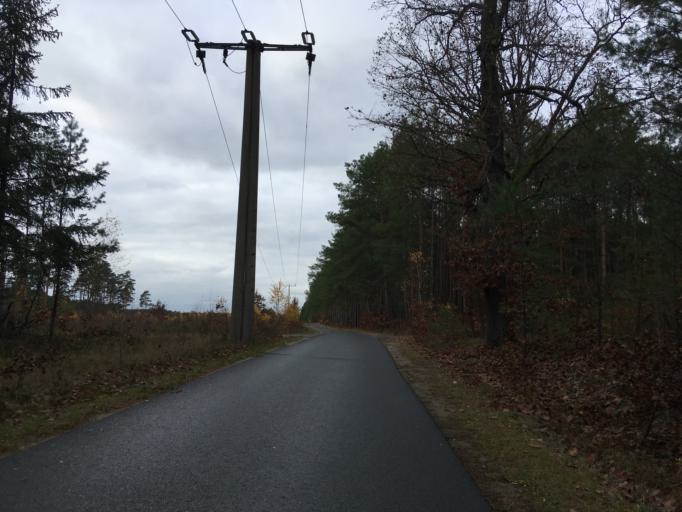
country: DE
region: Brandenburg
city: Jamlitz
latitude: 52.0789
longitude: 14.4570
